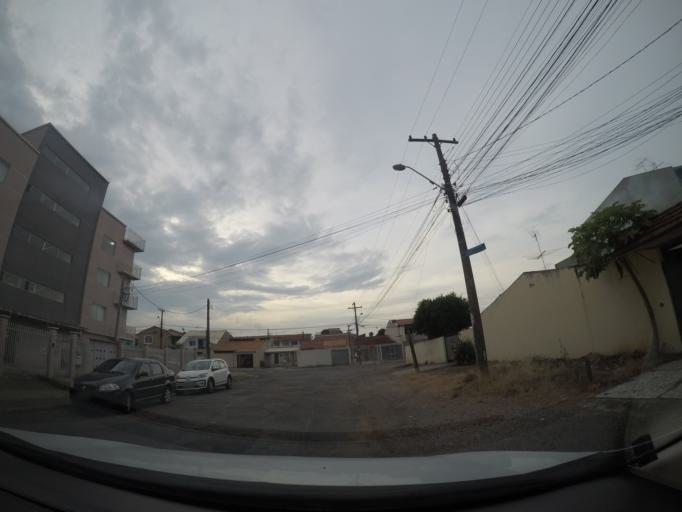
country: BR
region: Parana
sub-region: Sao Jose Dos Pinhais
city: Sao Jose dos Pinhais
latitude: -25.5213
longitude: -49.2333
